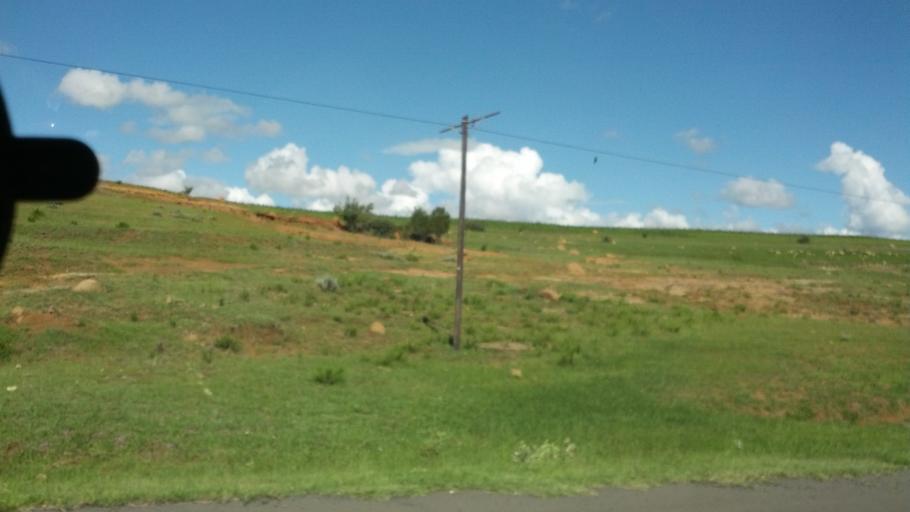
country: LS
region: Maseru
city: Maseru
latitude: -29.5145
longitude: 27.5242
